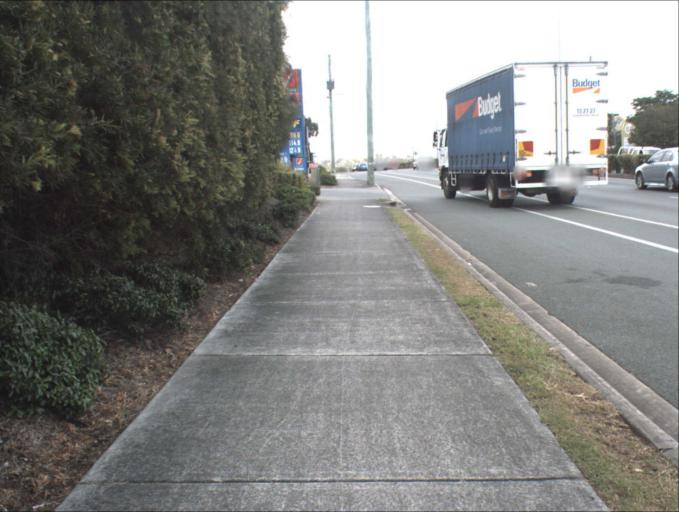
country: AU
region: Queensland
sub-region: Logan
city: Beenleigh
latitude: -27.7142
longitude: 153.1874
